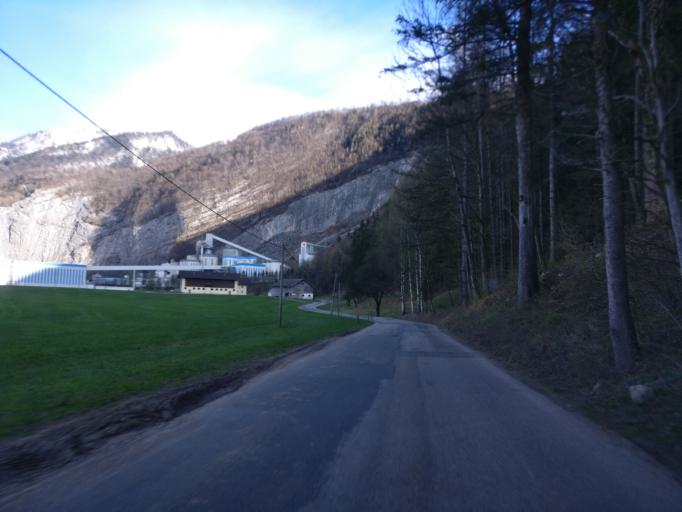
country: AT
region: Salzburg
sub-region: Politischer Bezirk Hallein
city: Golling an der Salzach
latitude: 47.5802
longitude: 13.1718
